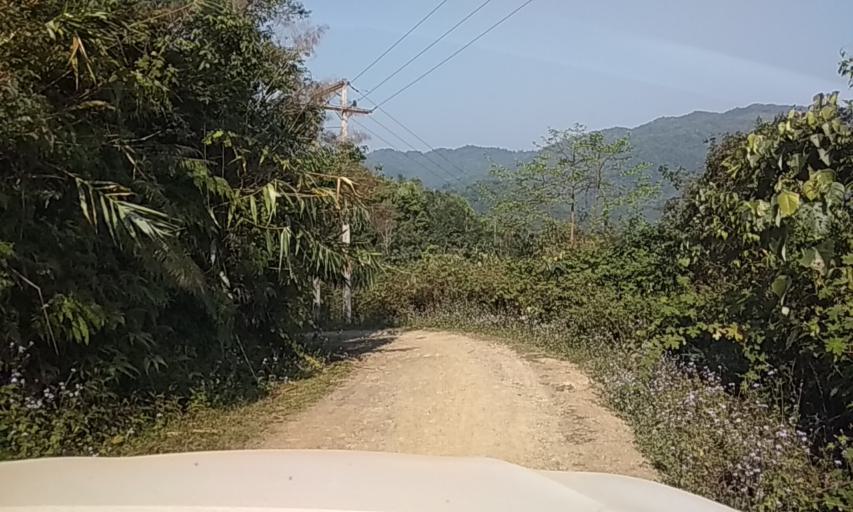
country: LA
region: Phongsali
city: Phongsali
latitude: 21.6975
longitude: 102.0658
